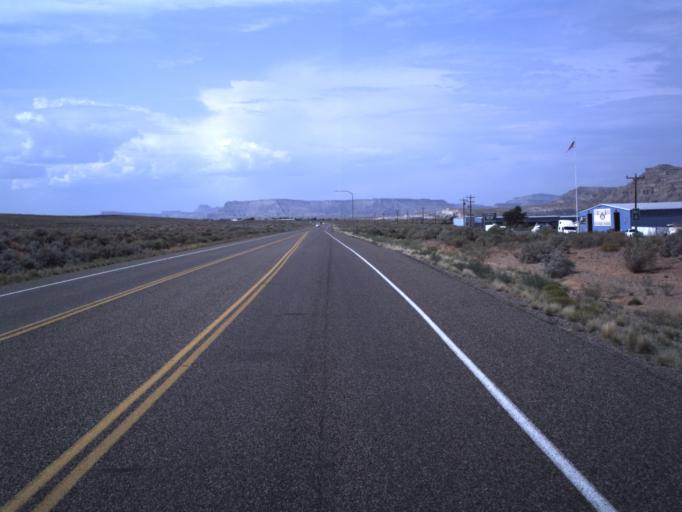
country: US
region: Arizona
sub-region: Coconino County
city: Page
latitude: 37.0649
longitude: -111.6456
